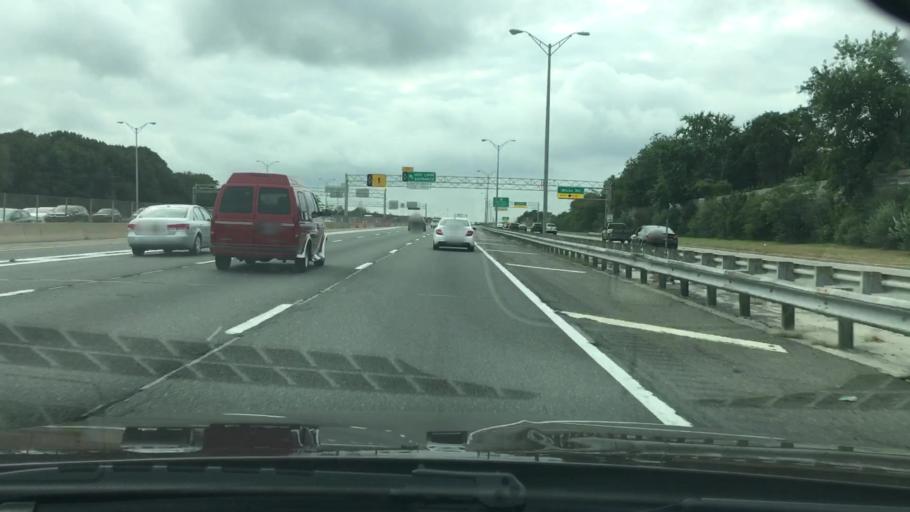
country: US
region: New York
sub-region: Suffolk County
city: Brentwood
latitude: 40.8056
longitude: -73.2617
